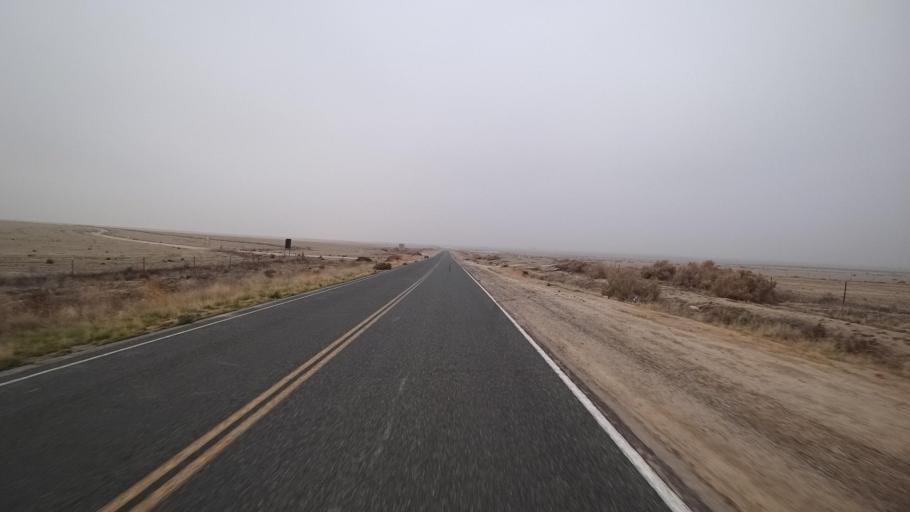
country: US
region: California
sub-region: Kern County
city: Buttonwillow
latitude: 35.3391
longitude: -119.4652
